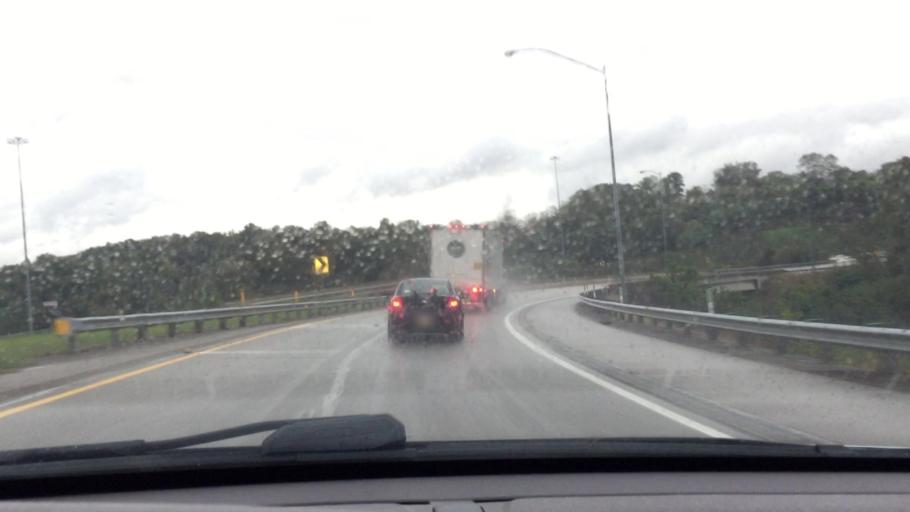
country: US
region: Pennsylvania
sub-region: Allegheny County
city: Carnegie
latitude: 40.4210
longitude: -80.1028
